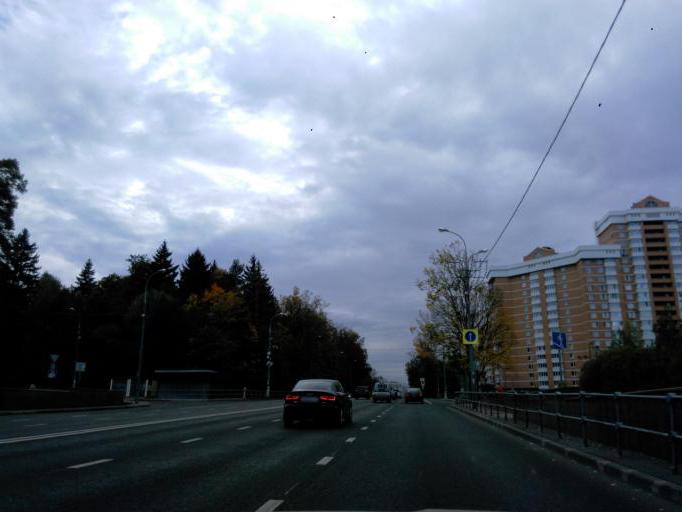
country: RU
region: Moscow
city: Zelenograd
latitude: 55.9888
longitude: 37.1837
